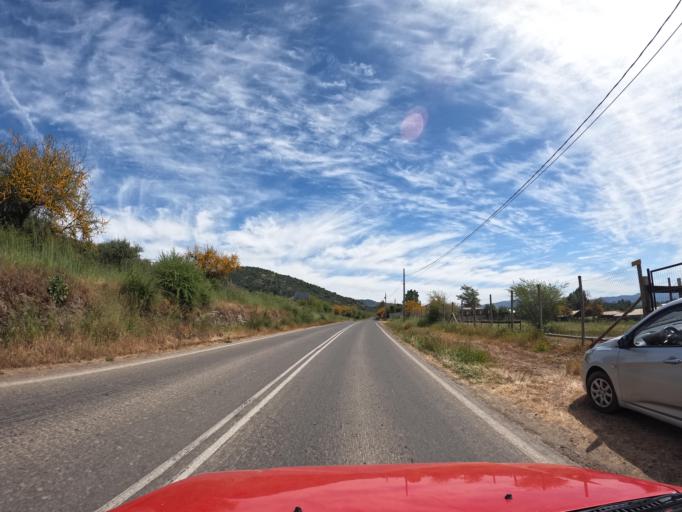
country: CL
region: Maule
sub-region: Provincia de Talca
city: Talca
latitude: -35.1198
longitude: -71.6466
